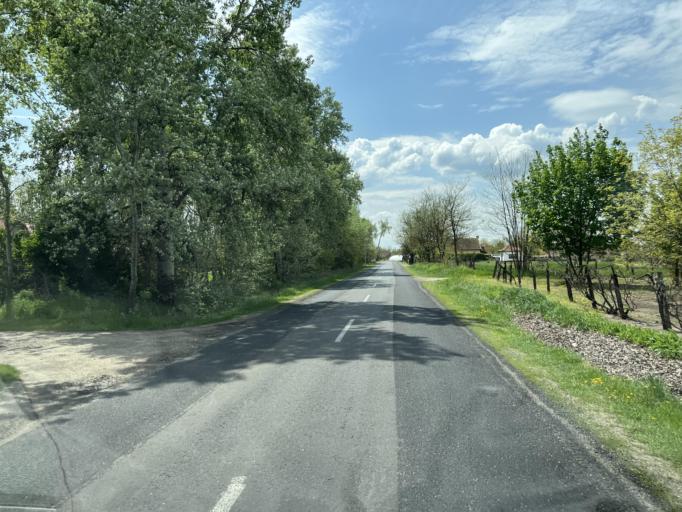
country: HU
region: Pest
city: Csemo
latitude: 47.1395
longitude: 19.7407
